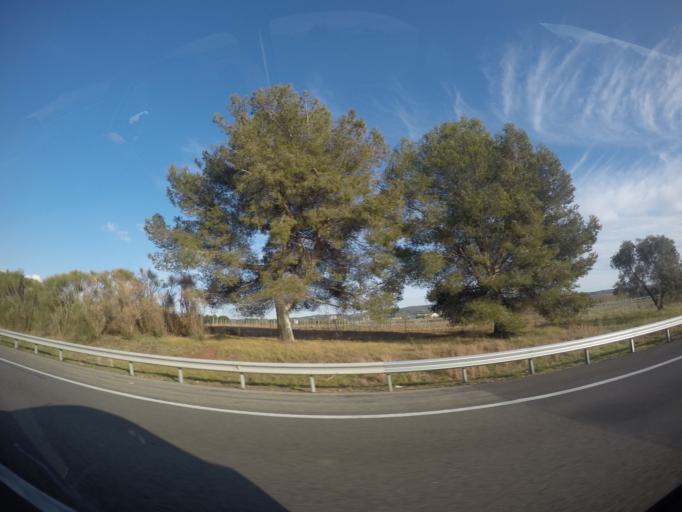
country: ES
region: Catalonia
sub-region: Provincia de Barcelona
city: Castellet
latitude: 41.3197
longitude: 1.6399
